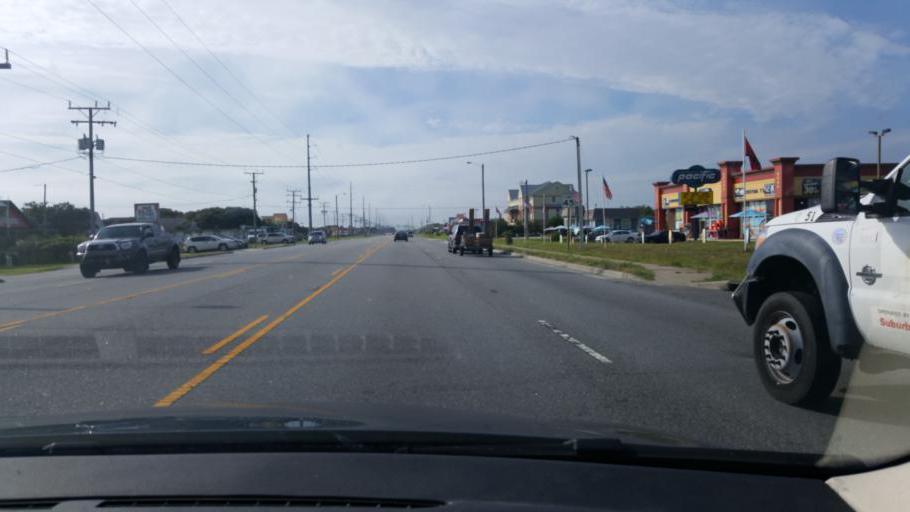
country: US
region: North Carolina
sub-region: Dare County
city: Kill Devil Hills
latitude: 36.0027
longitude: -75.6544
